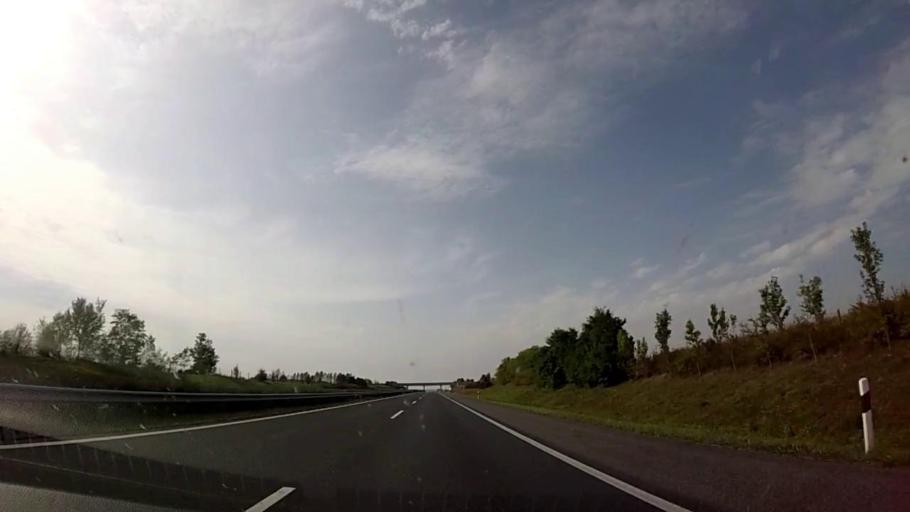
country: HU
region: Zala
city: Becsehely
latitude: 46.4365
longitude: 16.8004
